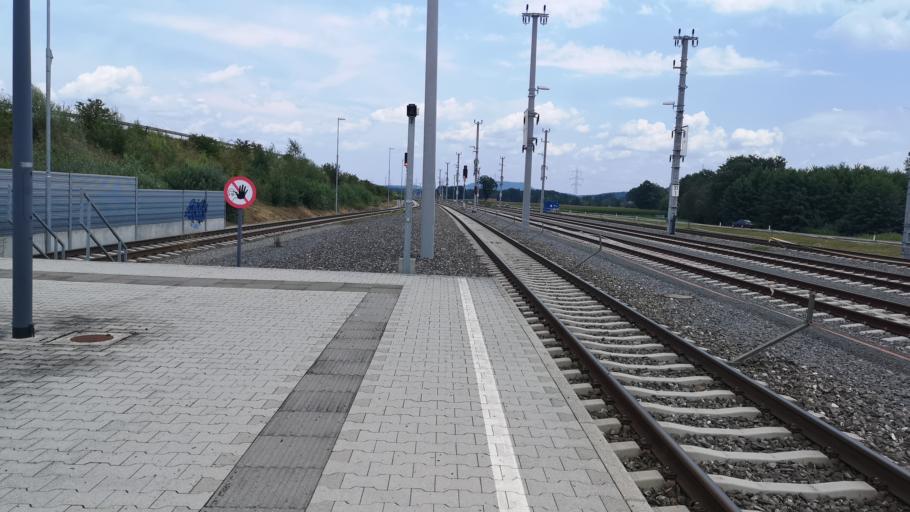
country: AT
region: Styria
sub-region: Politischer Bezirk Deutschlandsberg
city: Wettmannstatten
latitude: 46.8380
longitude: 15.3828
